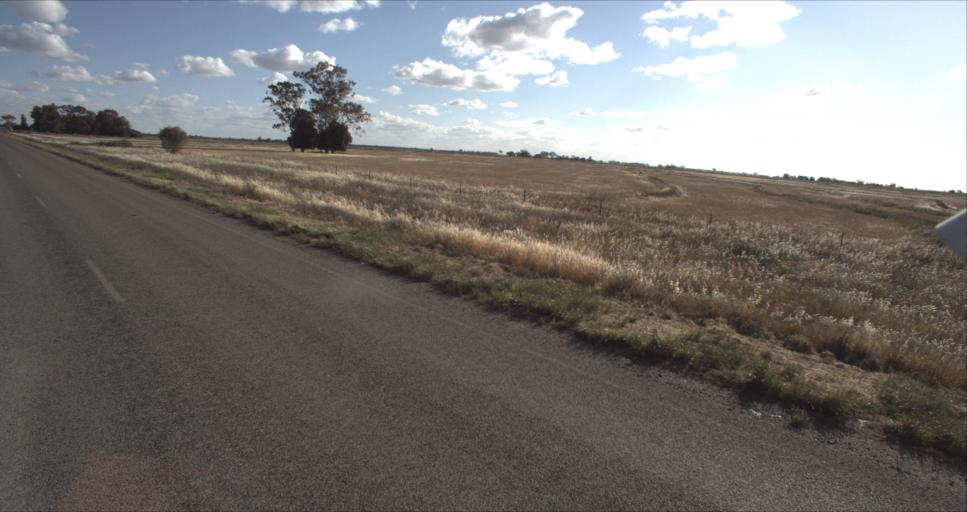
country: AU
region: New South Wales
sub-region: Leeton
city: Leeton
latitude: -34.5344
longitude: 146.2808
